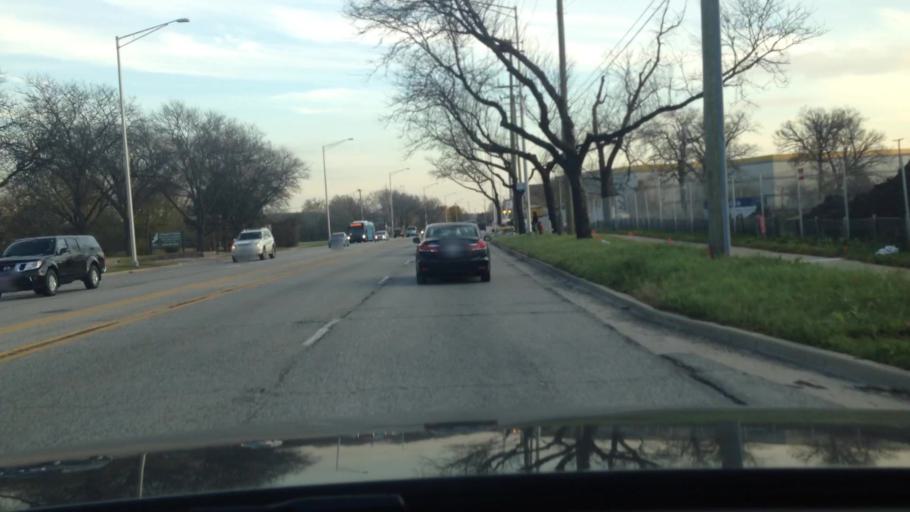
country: US
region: Illinois
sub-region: Cook County
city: Arlington Heights
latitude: 42.0497
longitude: -87.9916
